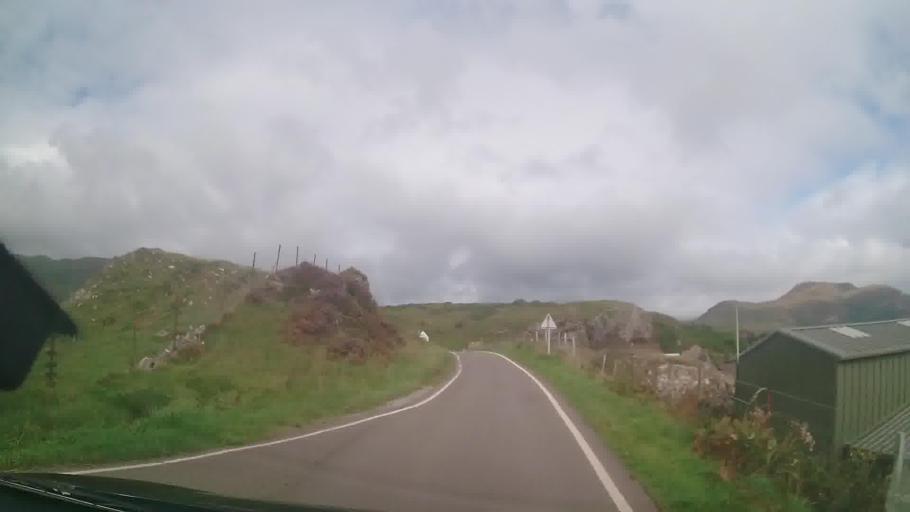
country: GB
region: Scotland
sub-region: Argyll and Bute
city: Isle Of Mull
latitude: 56.6908
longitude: -6.0952
